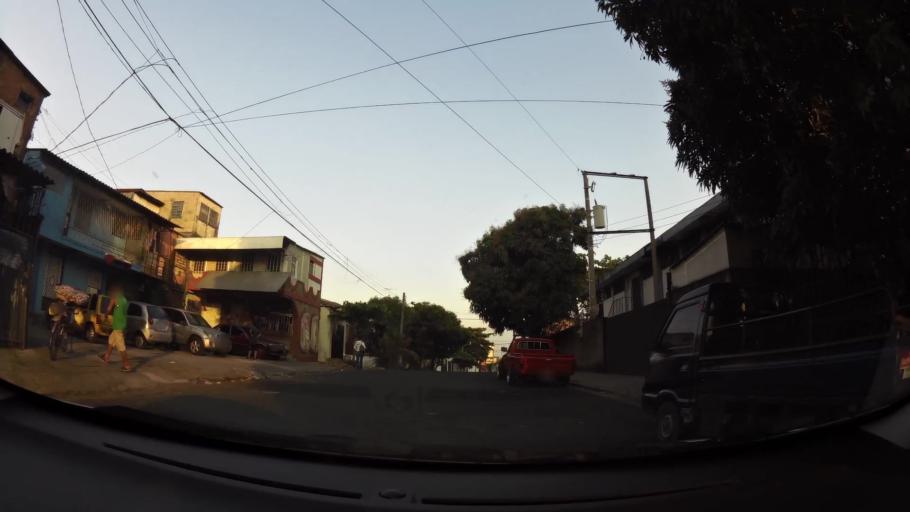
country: SV
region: San Salvador
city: Cuscatancingo
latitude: 13.7178
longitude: -89.1920
